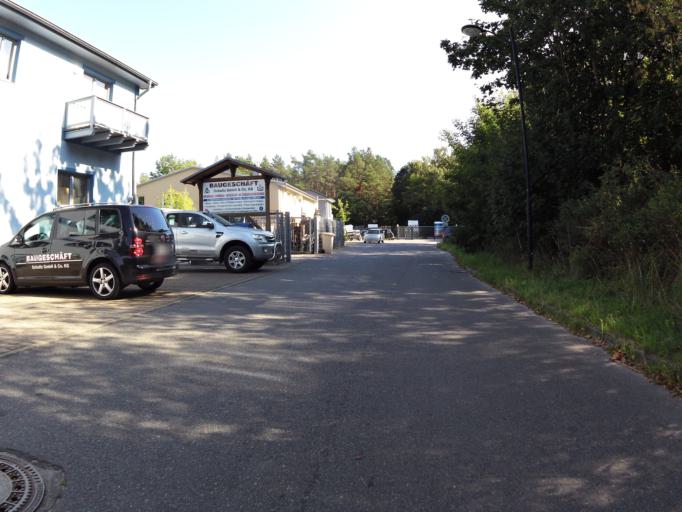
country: DE
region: Mecklenburg-Vorpommern
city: Seebad Heringsdorf
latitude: 53.9315
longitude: 14.1933
